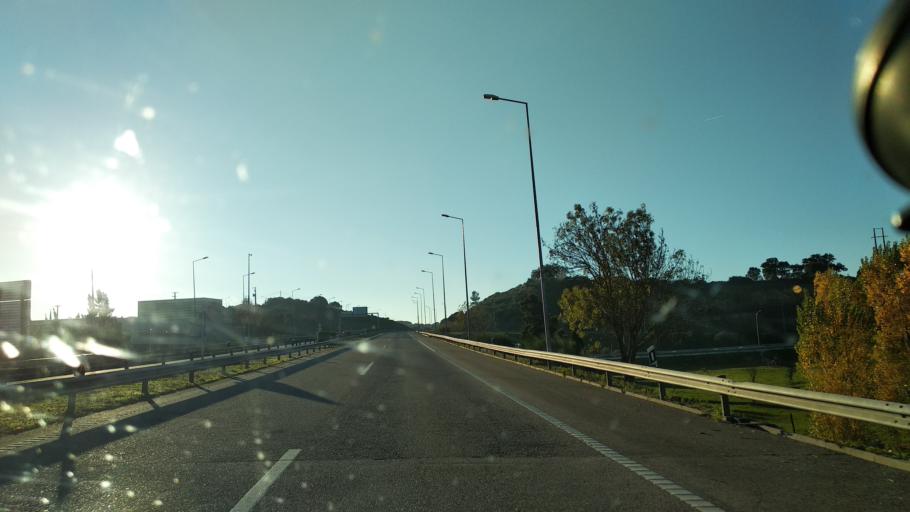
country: PT
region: Santarem
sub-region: Torres Novas
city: Torres Novas
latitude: 39.4653
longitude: -8.5299
